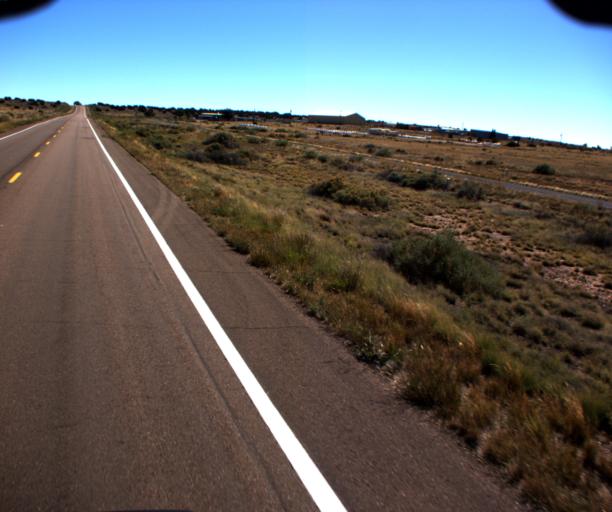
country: US
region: Arizona
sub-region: Apache County
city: Saint Johns
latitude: 34.5072
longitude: -109.4225
